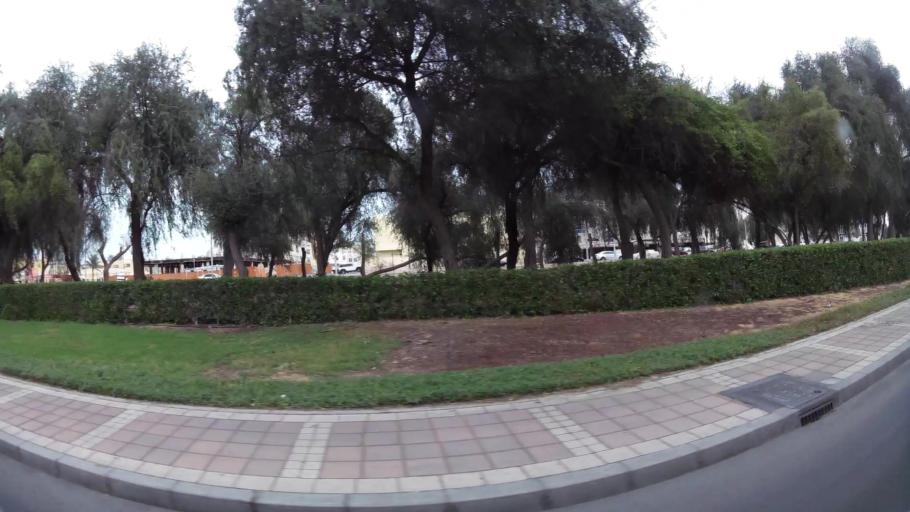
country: AE
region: Abu Dhabi
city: Abu Dhabi
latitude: 24.4374
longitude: 54.4028
